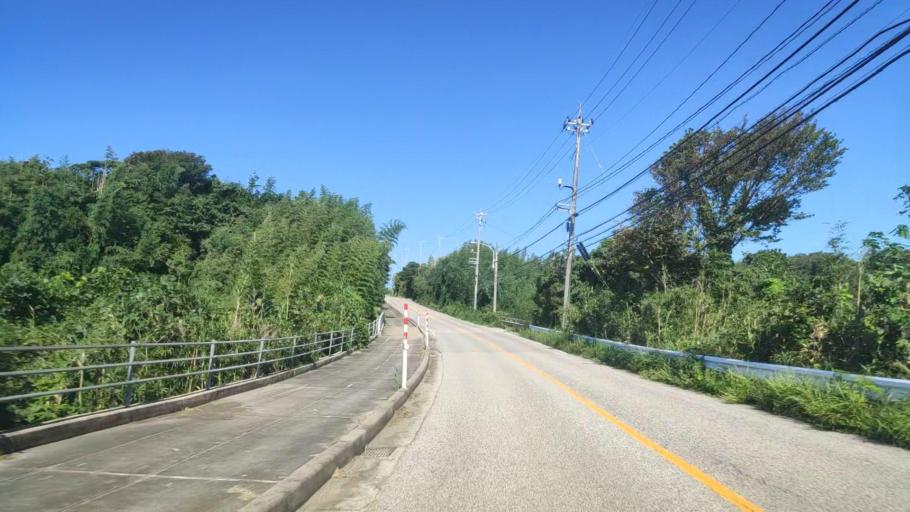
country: JP
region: Ishikawa
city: Hakui
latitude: 37.0511
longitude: 136.7347
